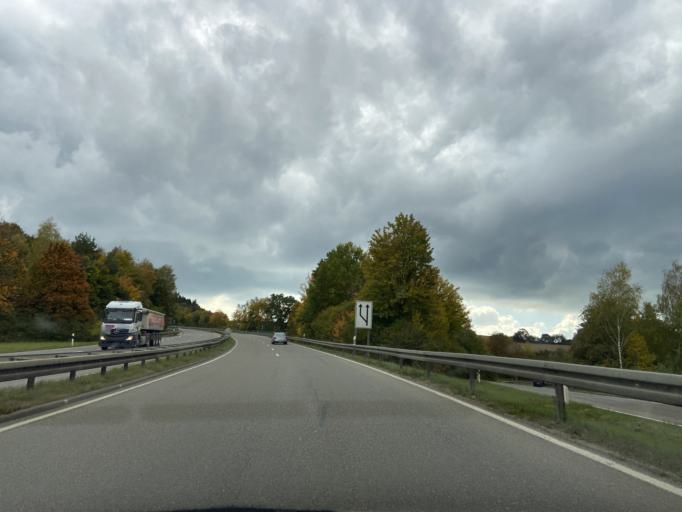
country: DE
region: Baden-Wuerttemberg
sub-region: Tuebingen Region
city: Sigmaringen
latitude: 48.0770
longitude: 9.2063
